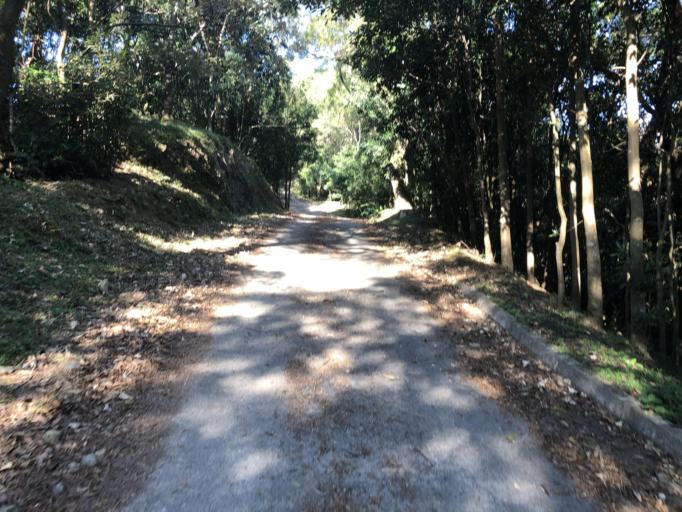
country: HK
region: Tsuen Wan
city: Tsuen Wan
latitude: 22.3962
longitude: 114.0879
